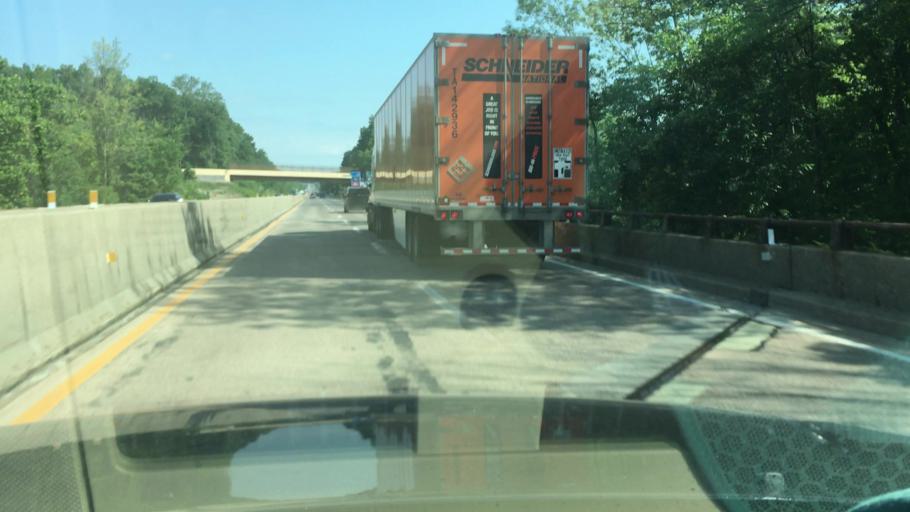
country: US
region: Pennsylvania
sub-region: Bucks County
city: Spinnerstown
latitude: 40.3938
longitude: -75.4109
